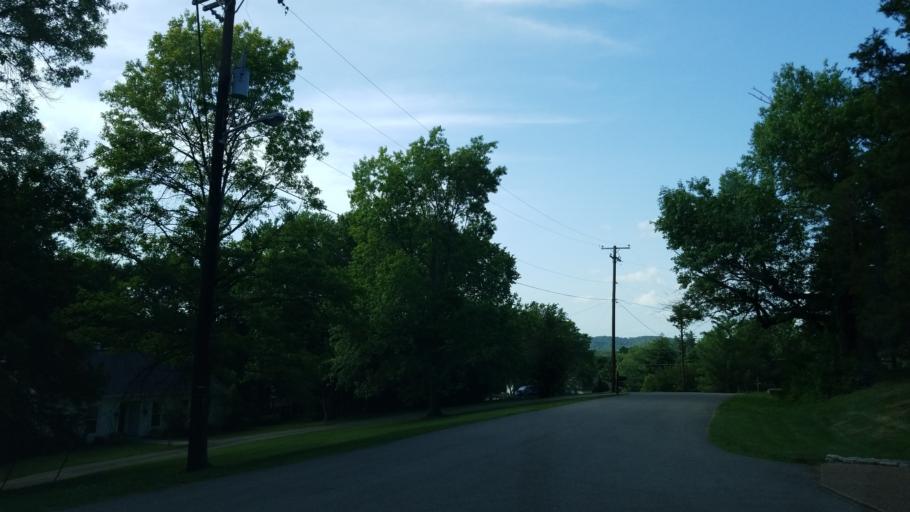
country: US
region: Tennessee
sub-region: Davidson County
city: Forest Hills
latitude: 36.0359
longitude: -86.8571
